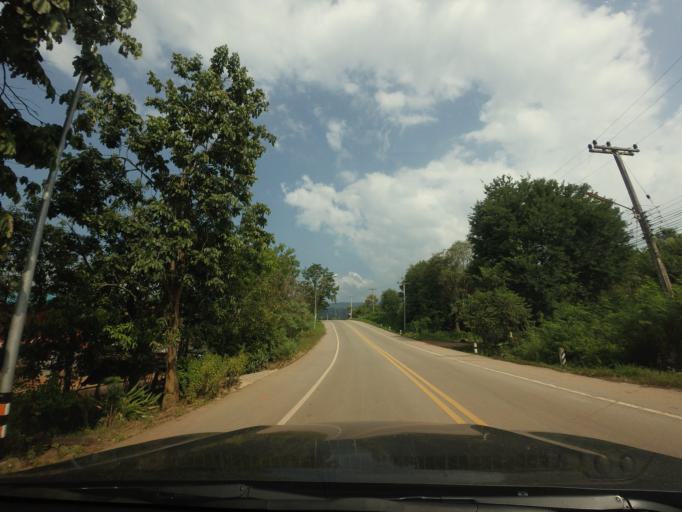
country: TH
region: Phitsanulok
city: Nakhon Thai
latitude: 17.0201
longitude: 100.9258
